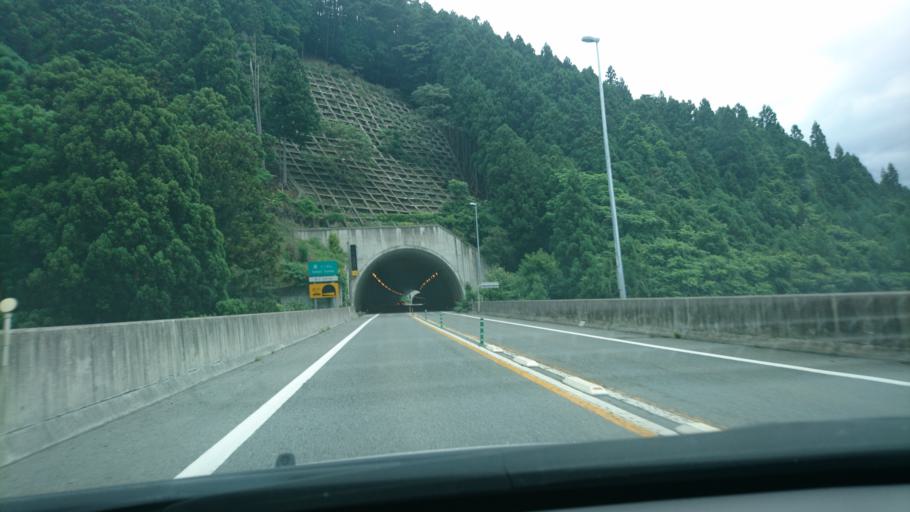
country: JP
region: Iwate
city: Ofunato
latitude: 39.0758
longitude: 141.7025
